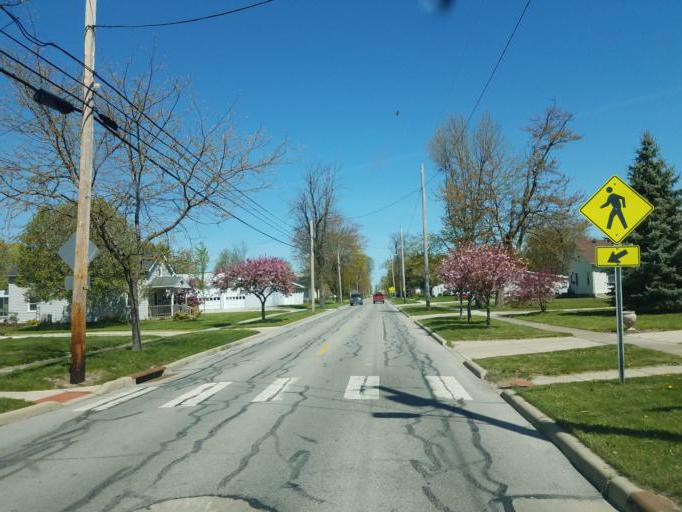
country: US
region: Ohio
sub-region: Ottawa County
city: Oak Harbor
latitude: 41.5132
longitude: -83.1450
